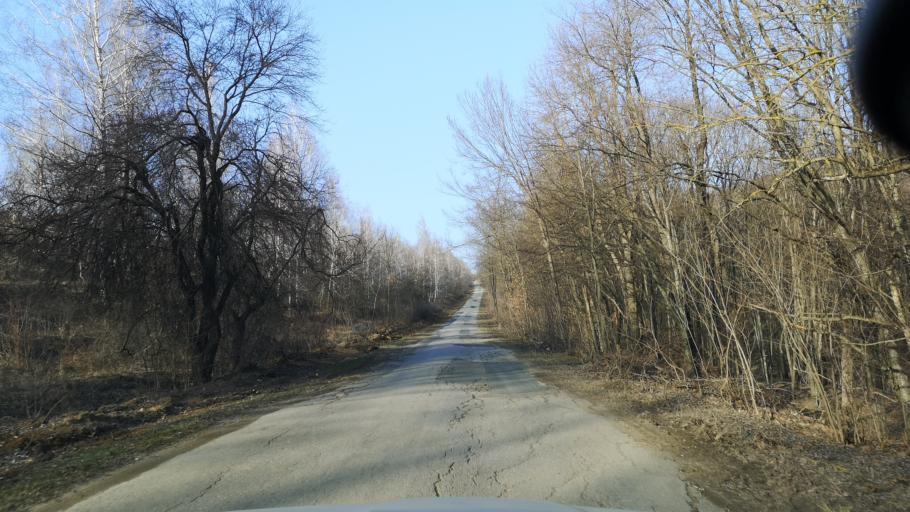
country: MD
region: Nisporeni
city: Nisporeni
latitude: 47.0934
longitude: 28.3157
